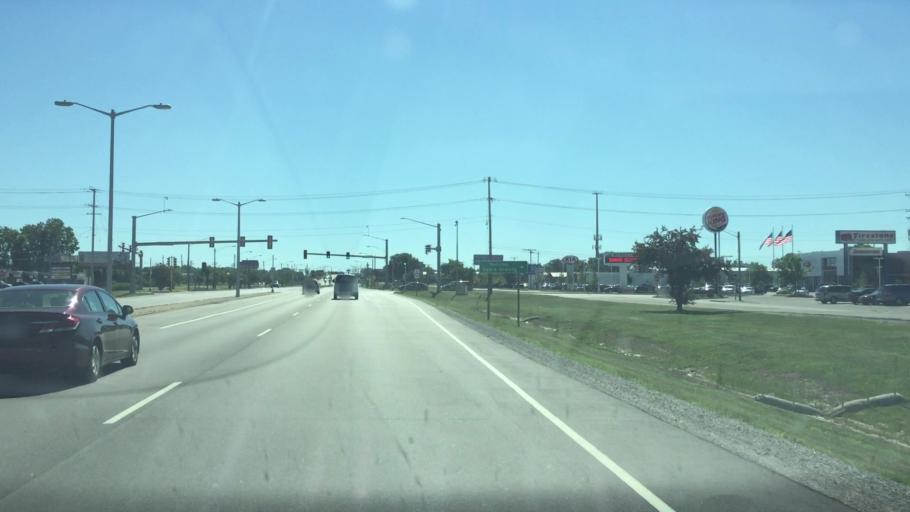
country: US
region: Wisconsin
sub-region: Outagamie County
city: Appleton
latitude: 44.2617
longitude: -88.4476
